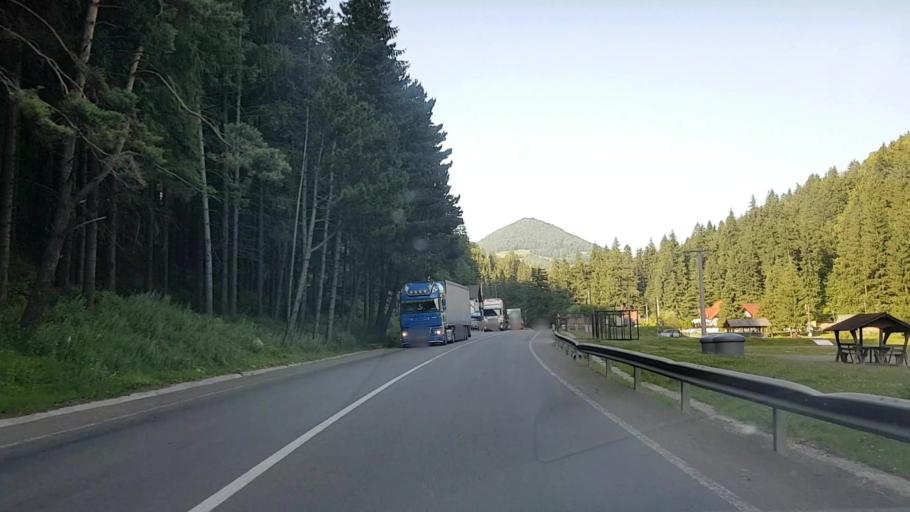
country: RO
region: Bistrita-Nasaud
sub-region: Comuna Tiha Bargaului
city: Tureac
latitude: 47.2173
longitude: 24.8937
